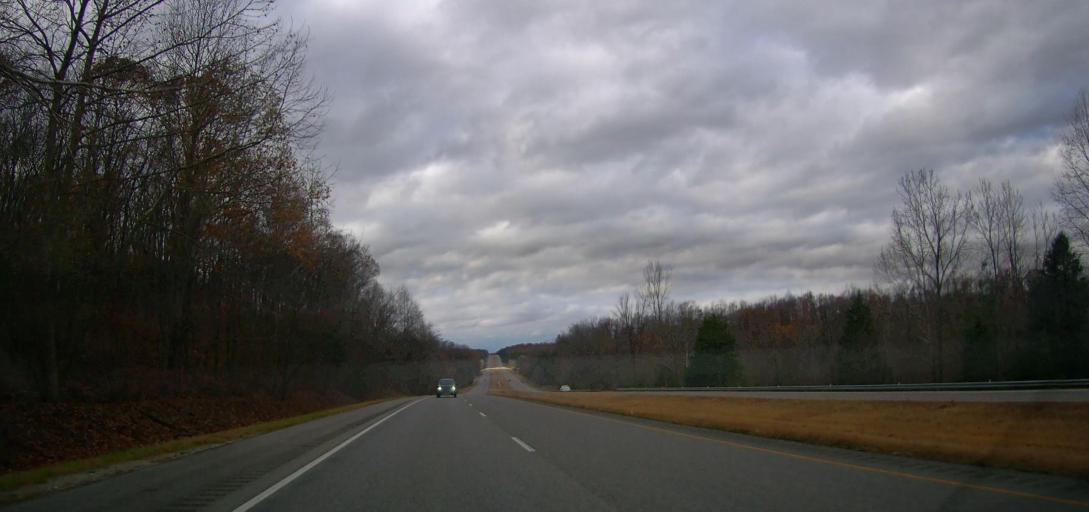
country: US
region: Alabama
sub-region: Lawrence County
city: Town Creek
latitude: 34.6034
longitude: -87.4481
